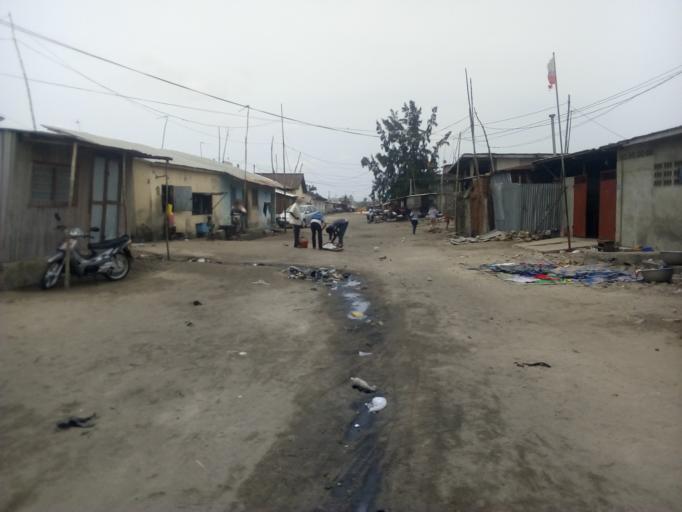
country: BJ
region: Littoral
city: Cotonou
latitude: 6.3868
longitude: 2.4340
